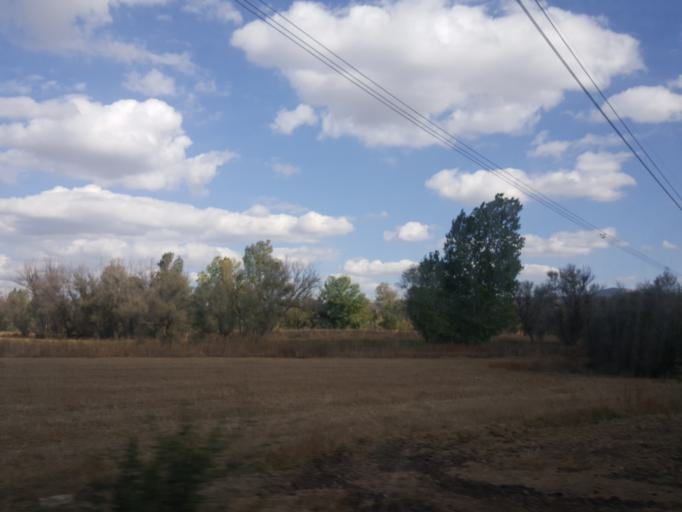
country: TR
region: Tokat
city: Yesilyurt
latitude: 40.0326
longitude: 36.2989
